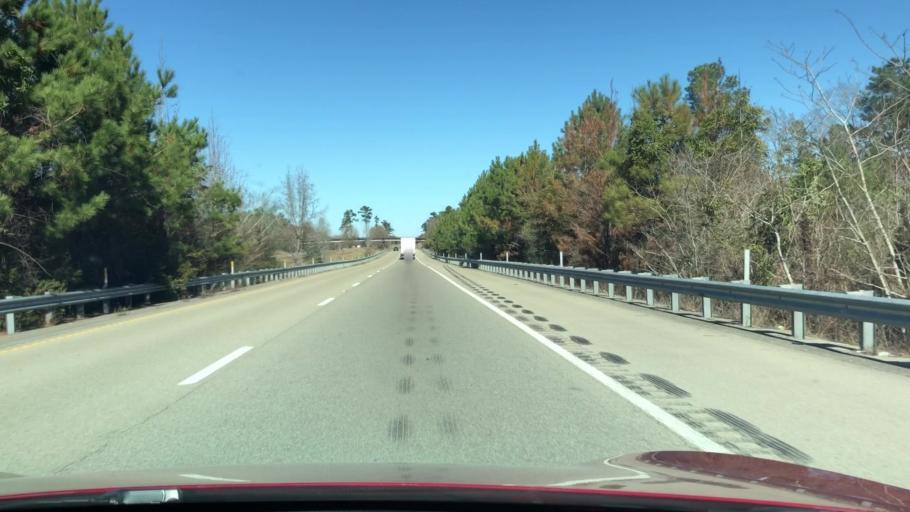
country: US
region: Mississippi
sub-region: Pearl River County
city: Poplarville
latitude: 30.7598
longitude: -89.5214
